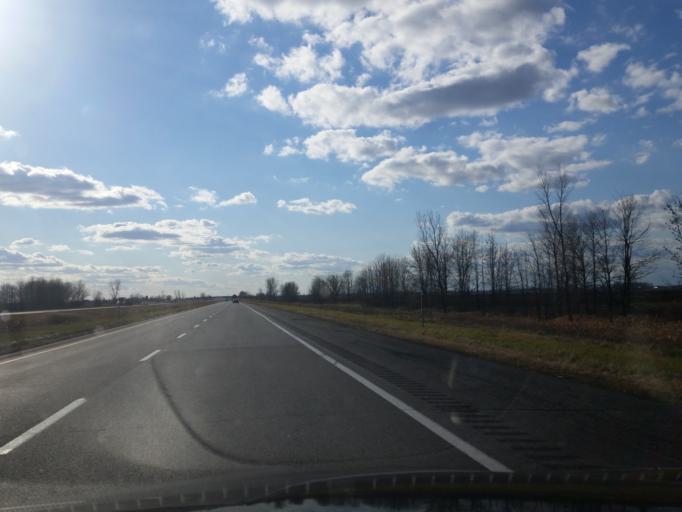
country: CA
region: Quebec
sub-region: Lanaudiere
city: Berthierville
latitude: 46.1552
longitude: -73.1012
